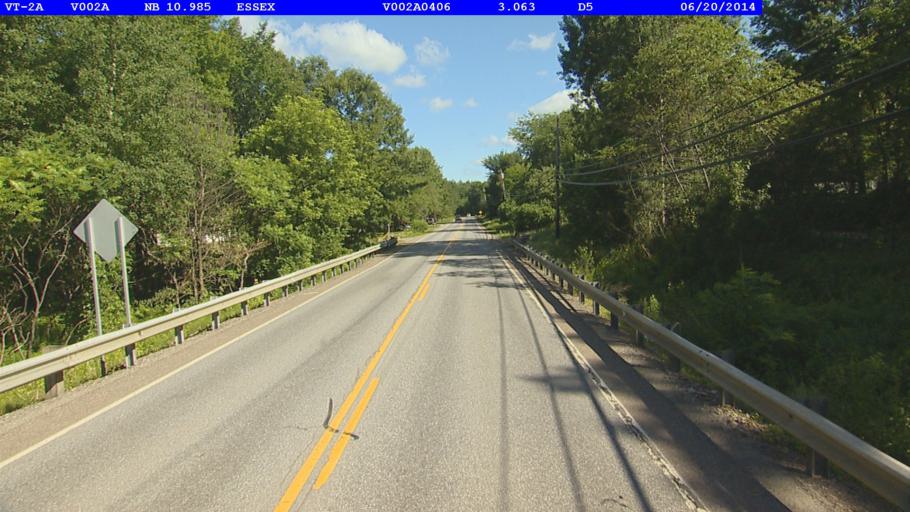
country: US
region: Vermont
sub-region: Chittenden County
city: Colchester
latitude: 44.5234
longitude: -73.1244
